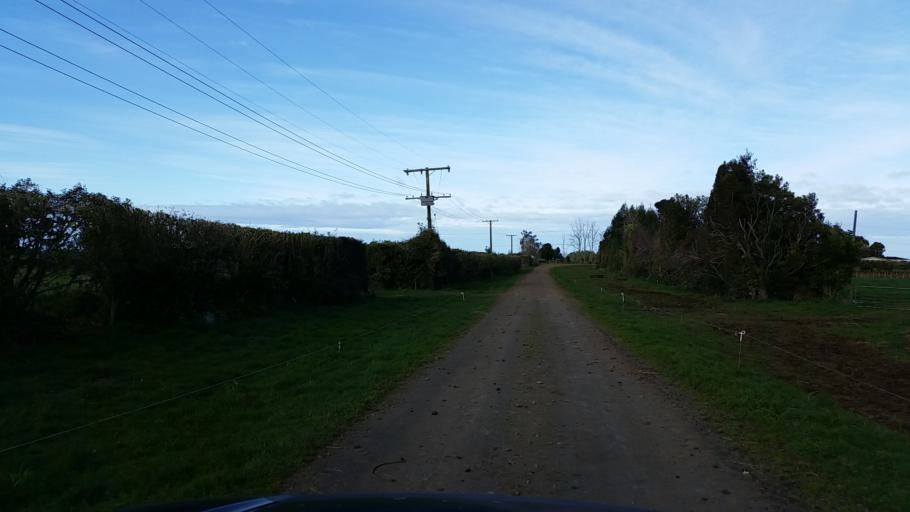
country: NZ
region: Taranaki
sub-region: South Taranaki District
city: Patea
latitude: -39.6591
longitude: 174.4972
